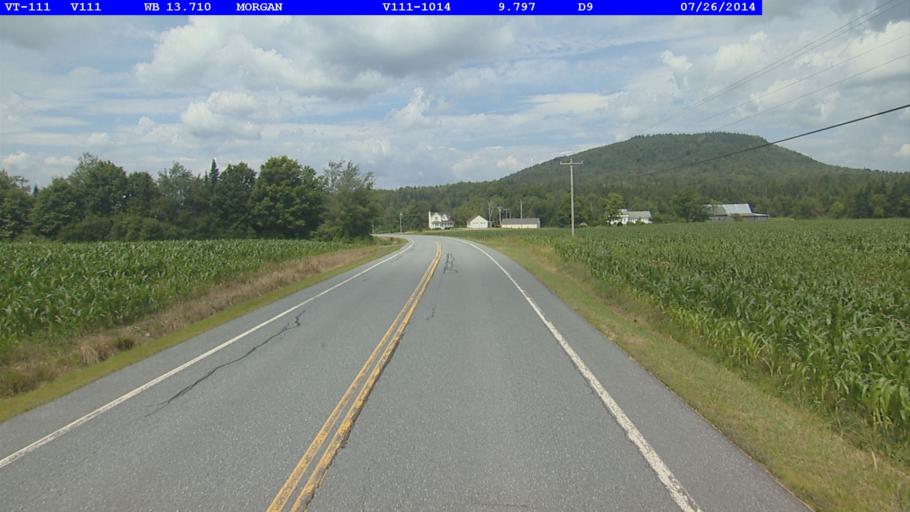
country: US
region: Vermont
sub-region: Orleans County
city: Newport
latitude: 44.8600
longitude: -71.9274
